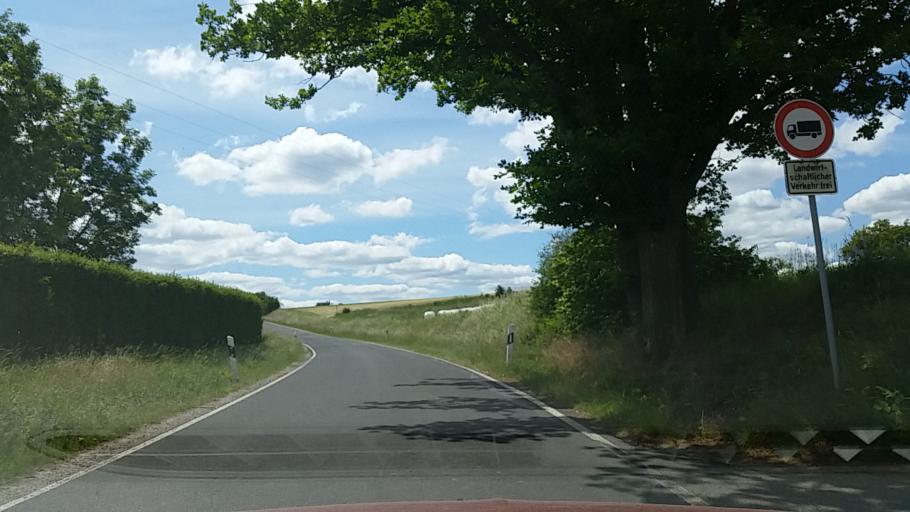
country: DE
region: Bavaria
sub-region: Regierungsbezirk Unterfranken
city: Neuendorf
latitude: 50.0090
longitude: 9.6562
